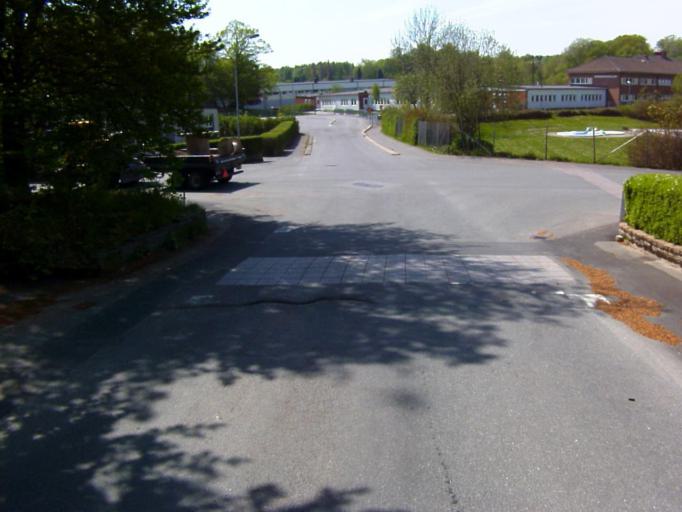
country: SE
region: Skane
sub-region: Kristianstads Kommun
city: Tollarp
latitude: 56.1724
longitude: 14.2878
